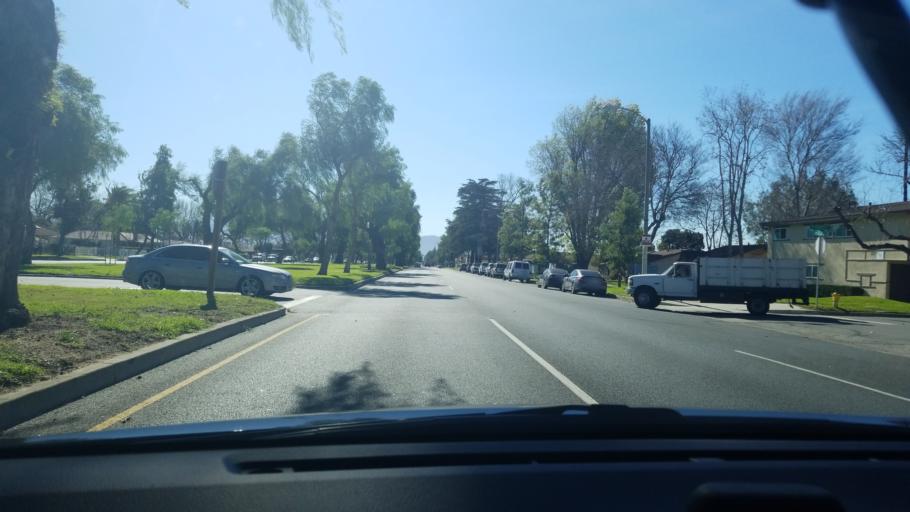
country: US
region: California
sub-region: San Bernardino County
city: Ontario
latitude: 34.0449
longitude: -117.6511
